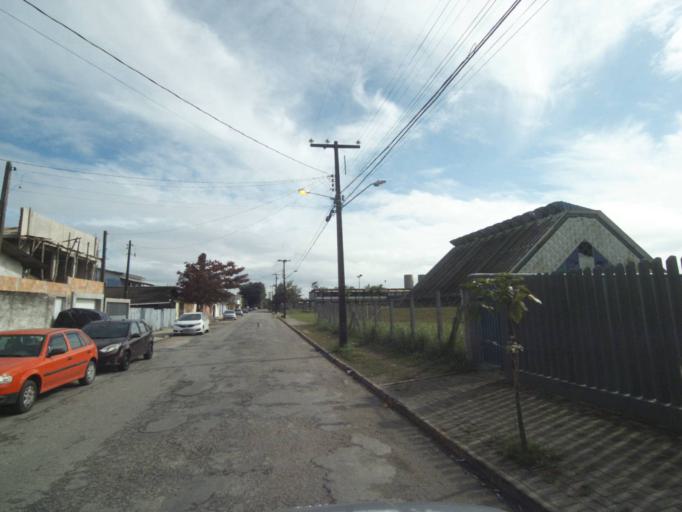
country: BR
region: Parana
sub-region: Paranagua
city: Paranagua
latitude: -25.5642
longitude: -48.5624
